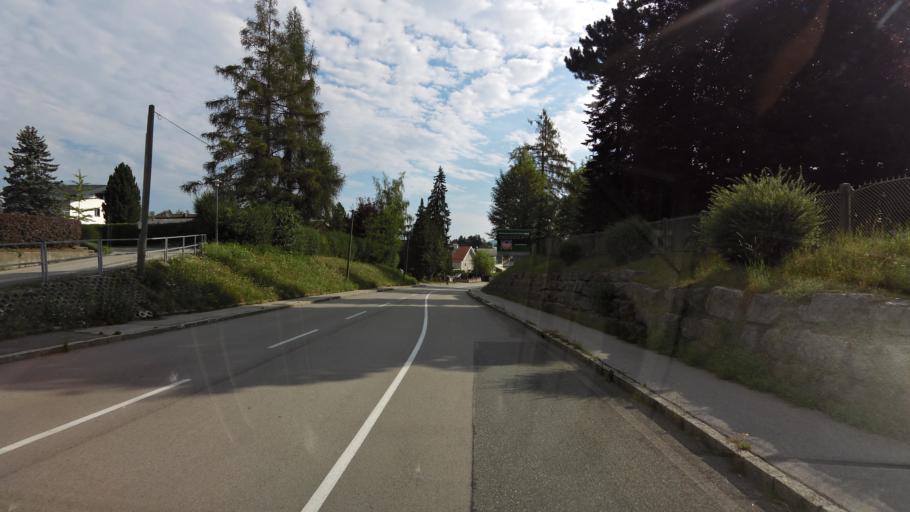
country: AT
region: Salzburg
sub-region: Politischer Bezirk Salzburg-Umgebung
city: Henndorf am Wallersee
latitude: 47.8954
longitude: 13.1830
